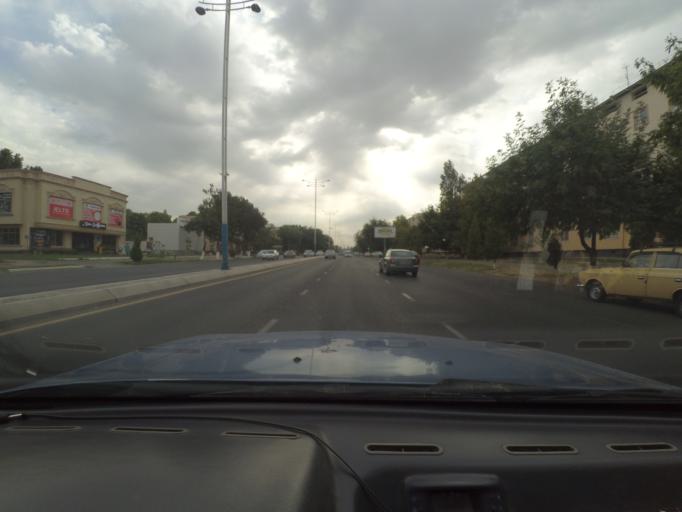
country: UZ
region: Toshkent
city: Salor
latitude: 41.3549
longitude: 69.3609
